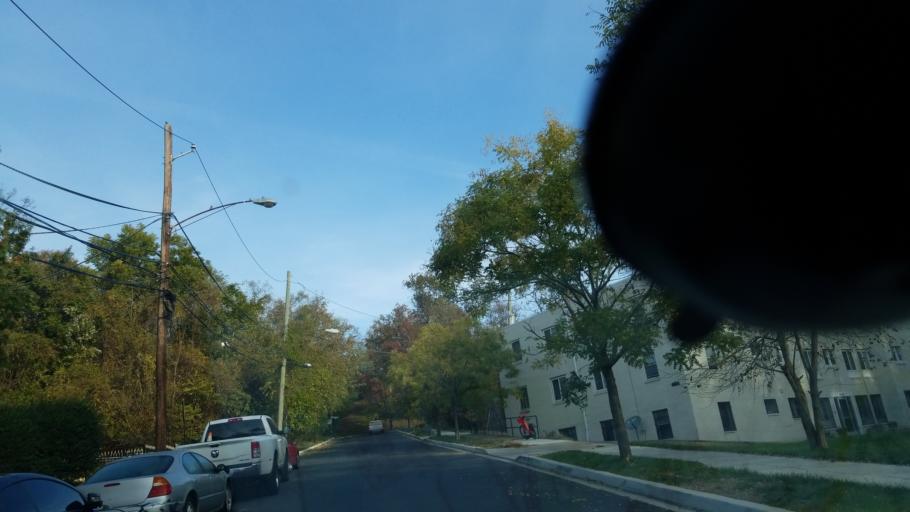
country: US
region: Maryland
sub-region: Prince George's County
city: Hillcrest Heights
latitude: 38.8541
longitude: -76.9828
